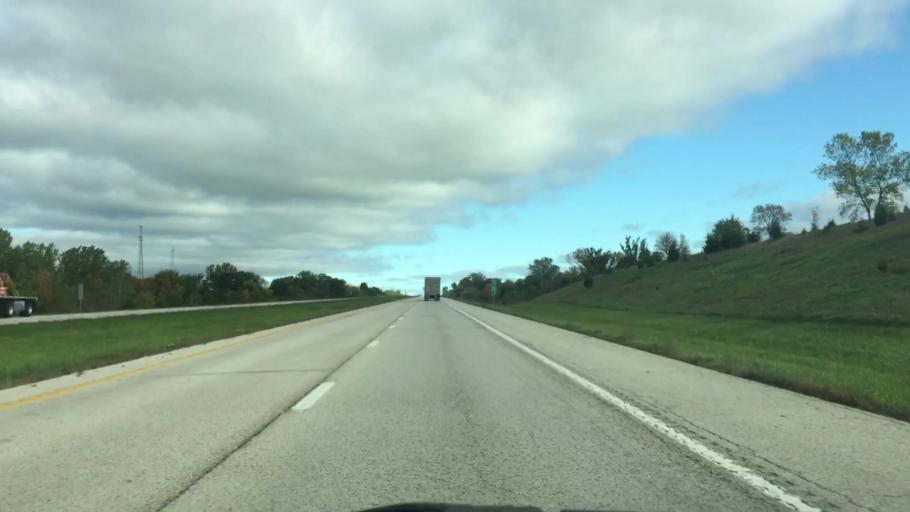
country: US
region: Missouri
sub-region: Harrison County
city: Bethany
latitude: 40.2382
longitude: -94.0127
